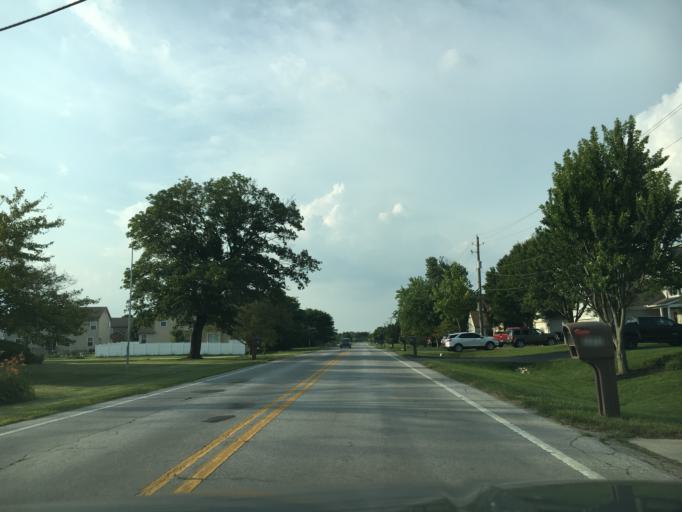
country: US
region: Ohio
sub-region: Franklin County
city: Hilliard
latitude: 40.0100
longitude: -83.1664
